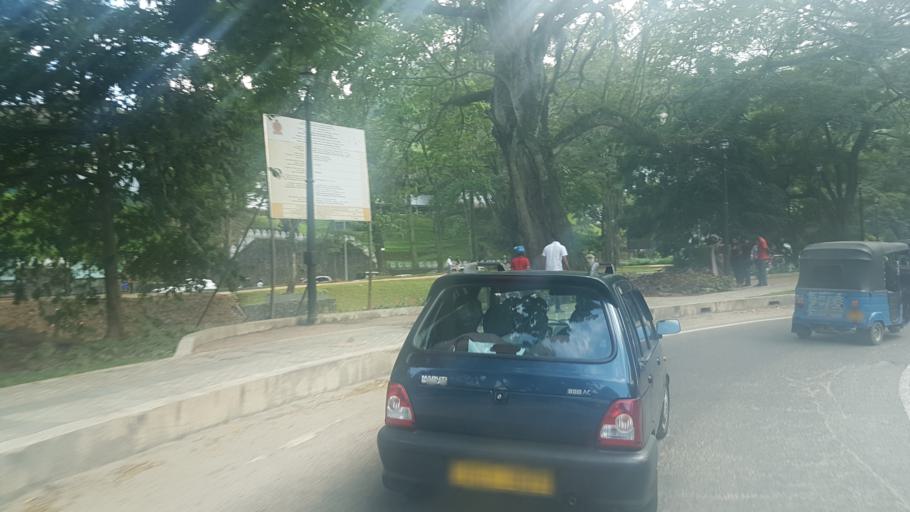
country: LK
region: Central
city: Kandy
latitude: 7.2882
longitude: 80.6451
